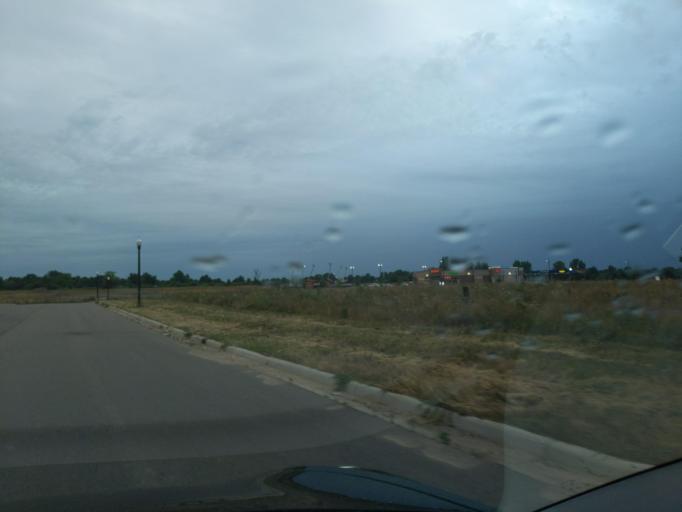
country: US
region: Michigan
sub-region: Clinton County
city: DeWitt
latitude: 42.8123
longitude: -84.5998
